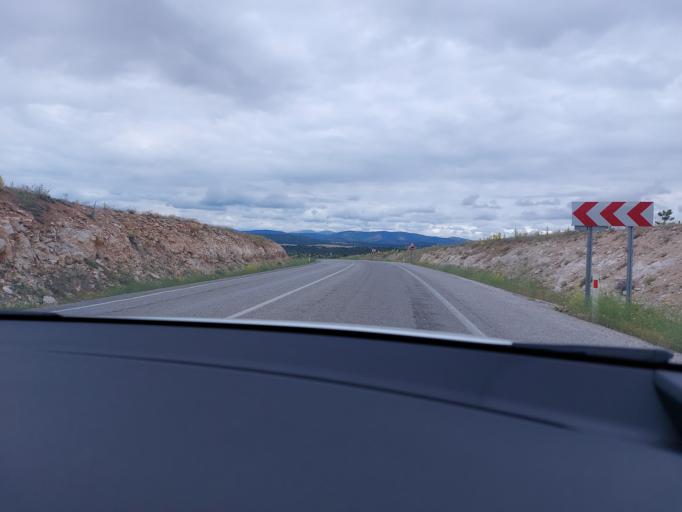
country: TR
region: Konya
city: Doganbey
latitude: 37.8828
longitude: 31.8384
